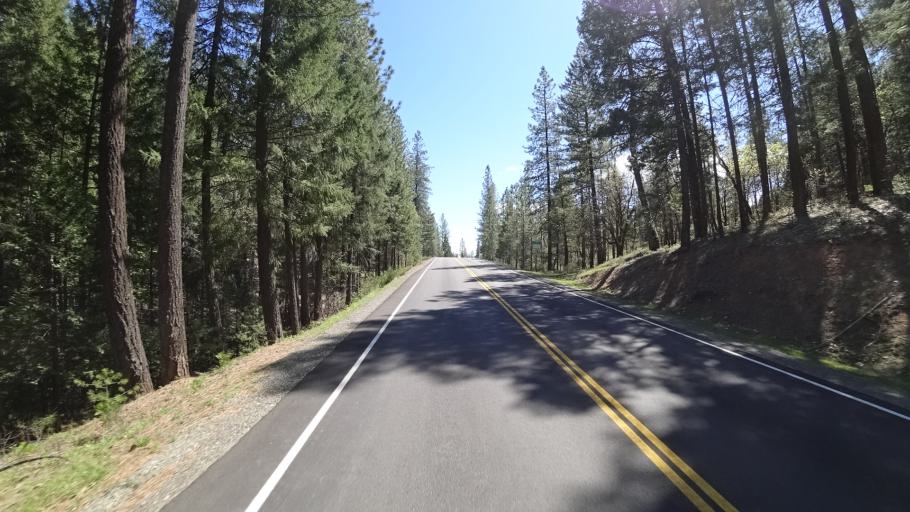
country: US
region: California
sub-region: Trinity County
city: Lewiston
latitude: 40.8841
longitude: -122.7961
